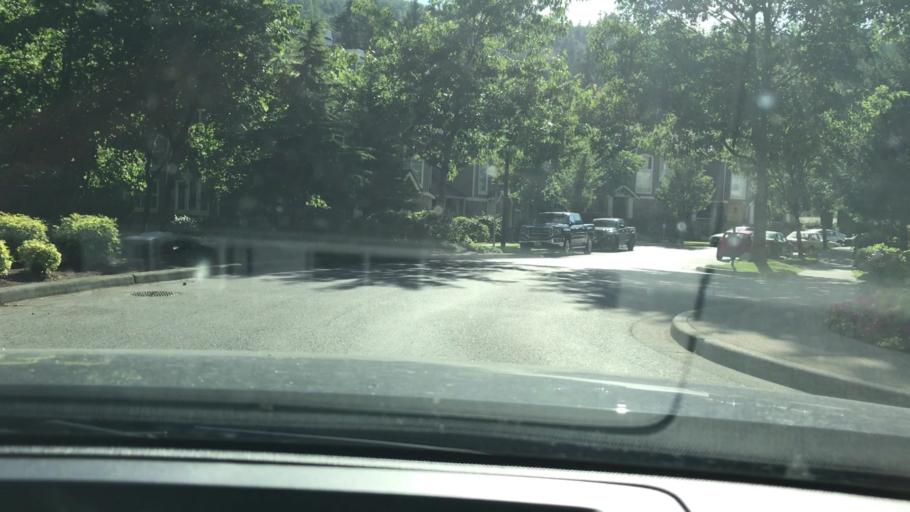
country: US
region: Washington
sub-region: King County
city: Issaquah
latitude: 47.5300
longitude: -122.0700
